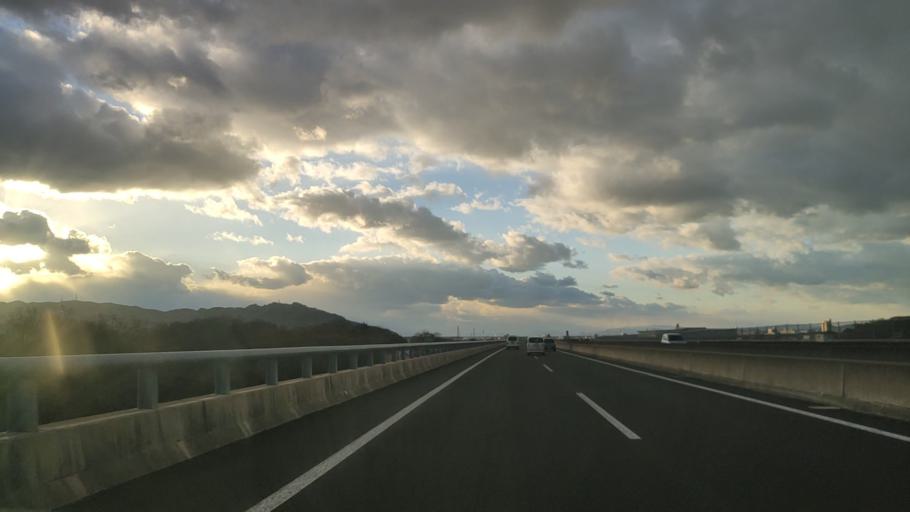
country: JP
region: Ehime
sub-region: Shikoku-chuo Shi
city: Matsuyama
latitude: 33.7883
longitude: 132.8109
